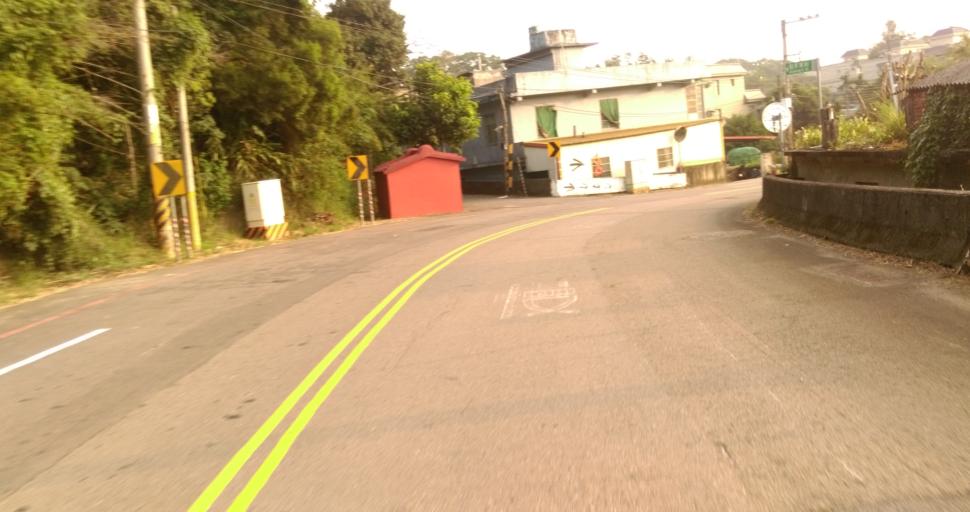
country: TW
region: Taiwan
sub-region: Hsinchu
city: Hsinchu
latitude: 24.7482
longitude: 120.9376
